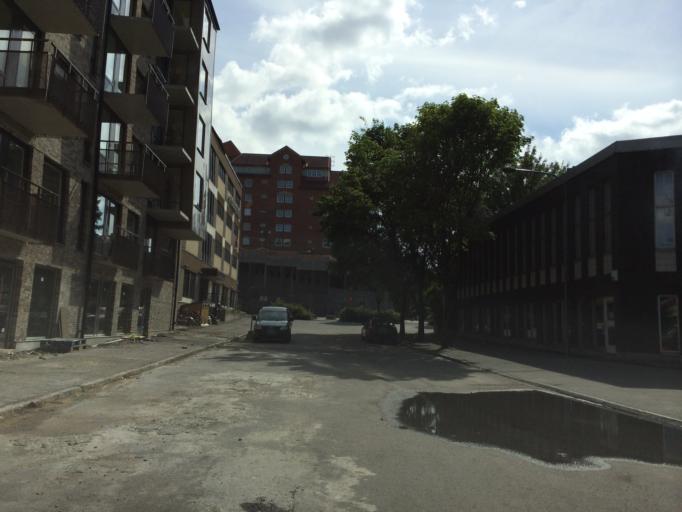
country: SE
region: Stockholm
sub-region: Stockholms Kommun
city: Arsta
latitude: 59.3132
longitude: 18.0251
